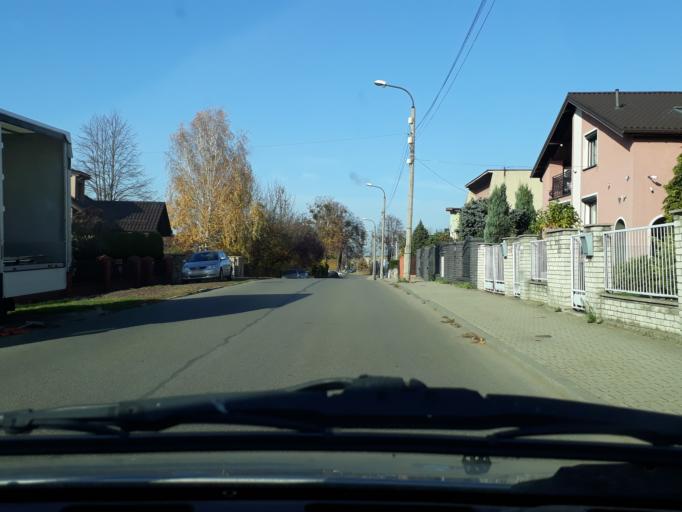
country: PL
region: Silesian Voivodeship
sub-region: Powiat tarnogorski
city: Tarnowskie Gory
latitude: 50.4274
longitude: 18.8733
